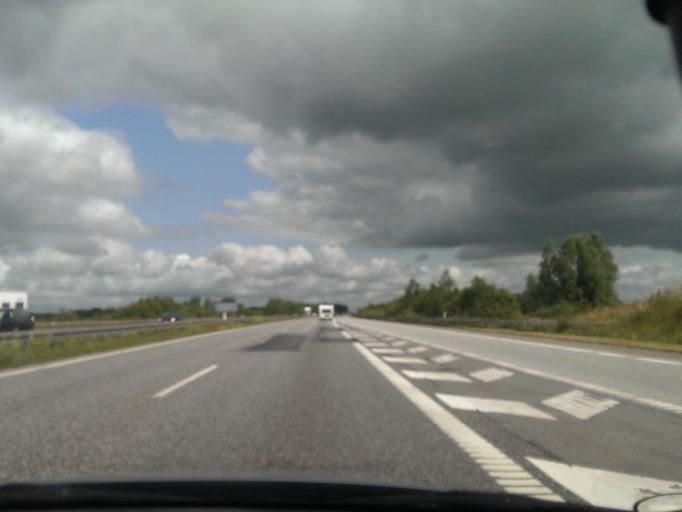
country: DK
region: North Denmark
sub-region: Mariagerfjord Kommune
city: Hobro
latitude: 56.6273
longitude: 9.7334
